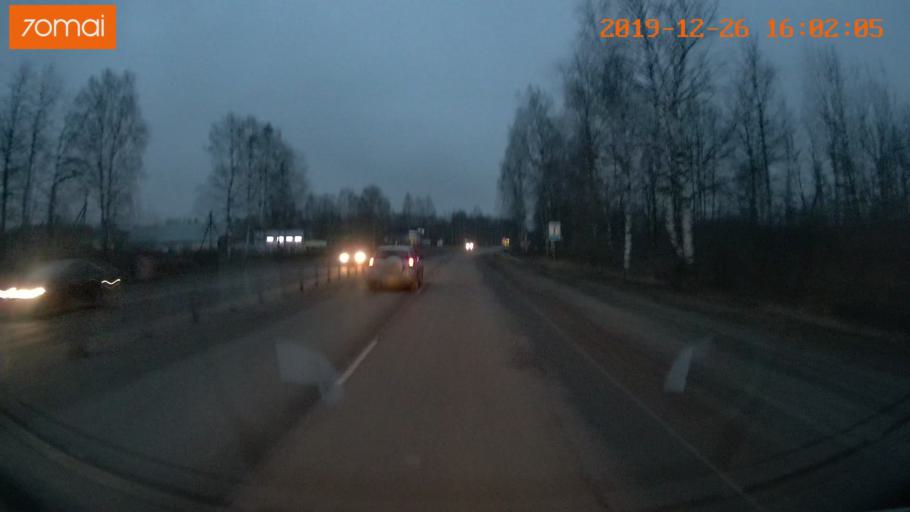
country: RU
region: Jaroslavl
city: Rybinsk
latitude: 58.0141
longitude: 38.8274
